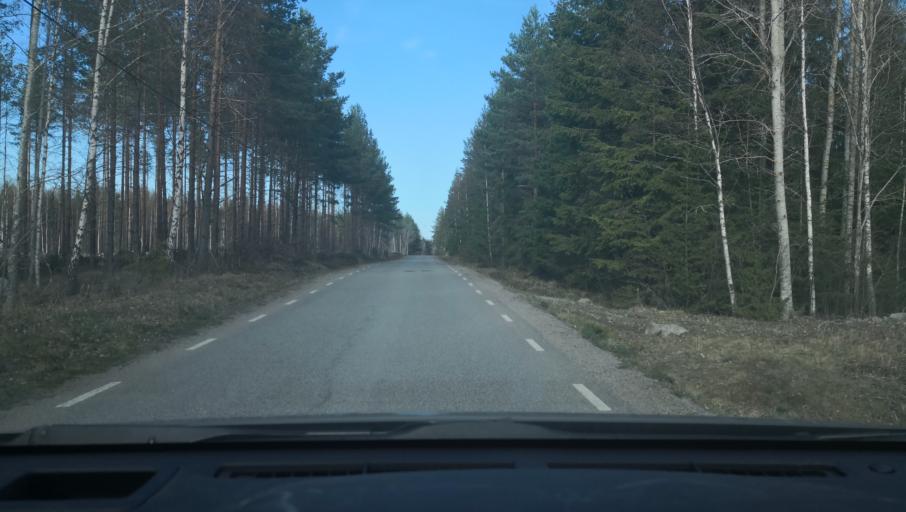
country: SE
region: Uppsala
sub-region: Heby Kommun
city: Heby
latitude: 59.9170
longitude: 16.8379
